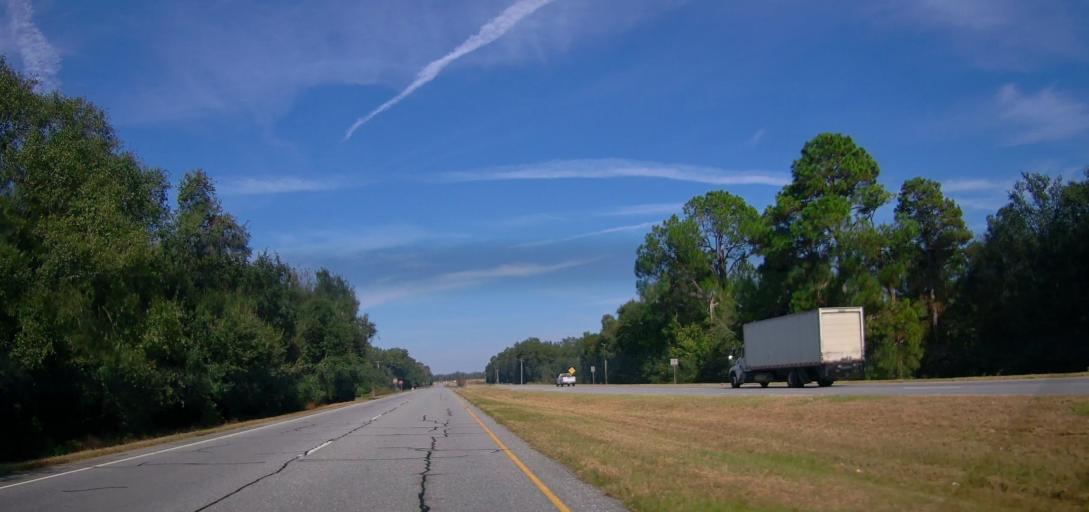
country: US
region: Georgia
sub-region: Dougherty County
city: Putney
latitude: 31.3523
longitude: -84.1615
